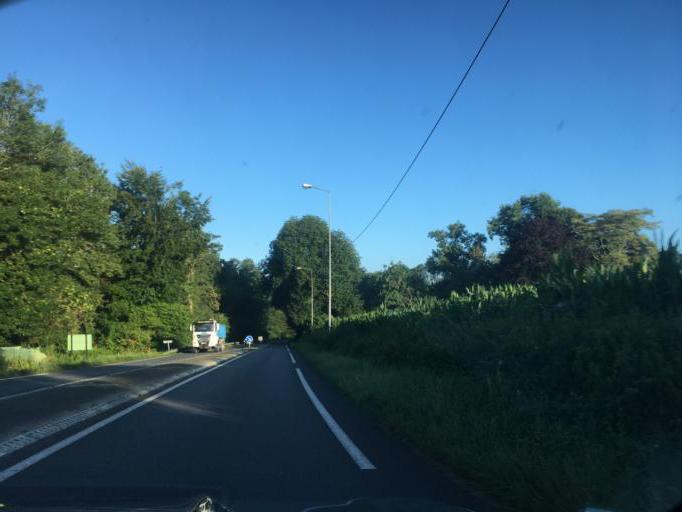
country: FR
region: Aquitaine
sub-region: Departement des Pyrenees-Atlantiques
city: Soumoulou
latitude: 43.2591
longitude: -0.1626
